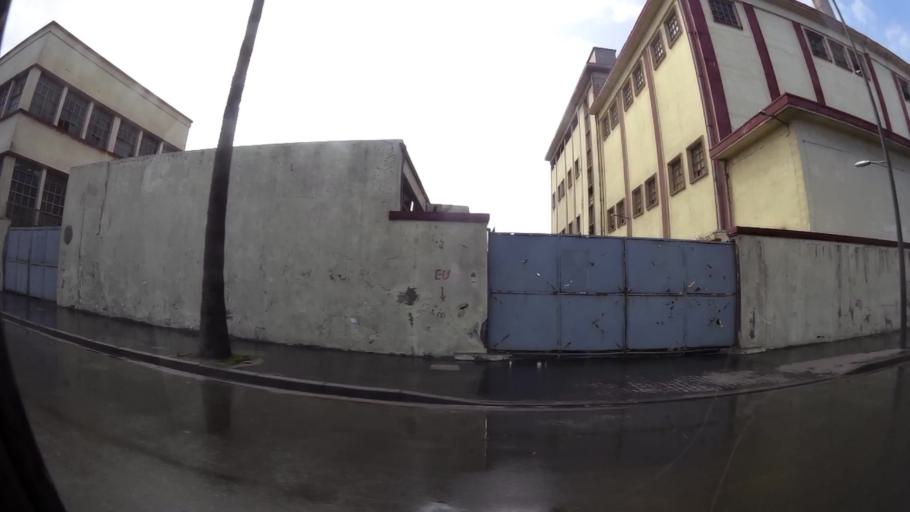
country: MA
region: Grand Casablanca
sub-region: Casablanca
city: Casablanca
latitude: 33.6077
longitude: -7.5700
